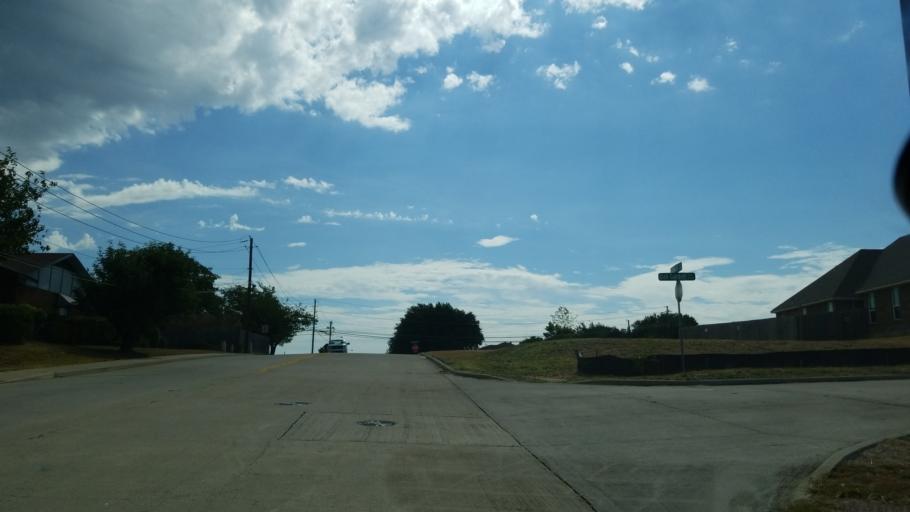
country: US
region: Texas
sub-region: Dallas County
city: Duncanville
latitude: 32.6549
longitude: -96.8499
